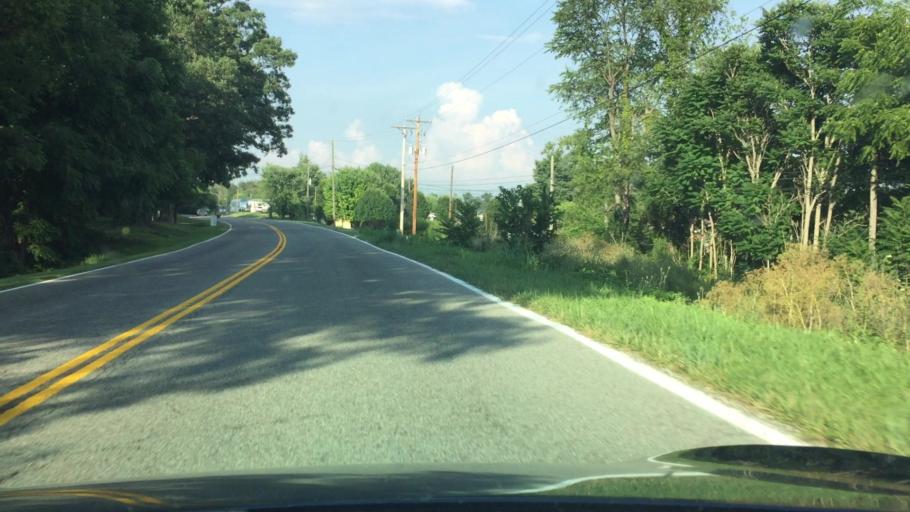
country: US
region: Virginia
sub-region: Pulaski County
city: Pulaski
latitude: 36.9576
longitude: -80.8627
